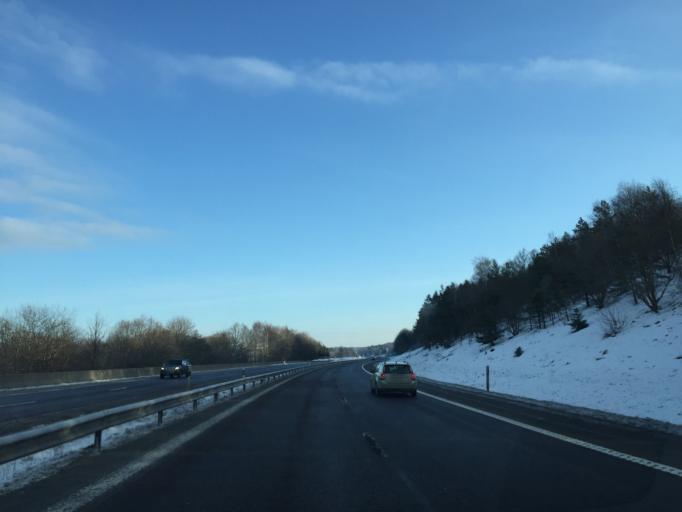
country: SE
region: Vaestra Goetaland
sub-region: Stenungsunds Kommun
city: Stora Hoga
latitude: 58.0455
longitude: 11.8527
